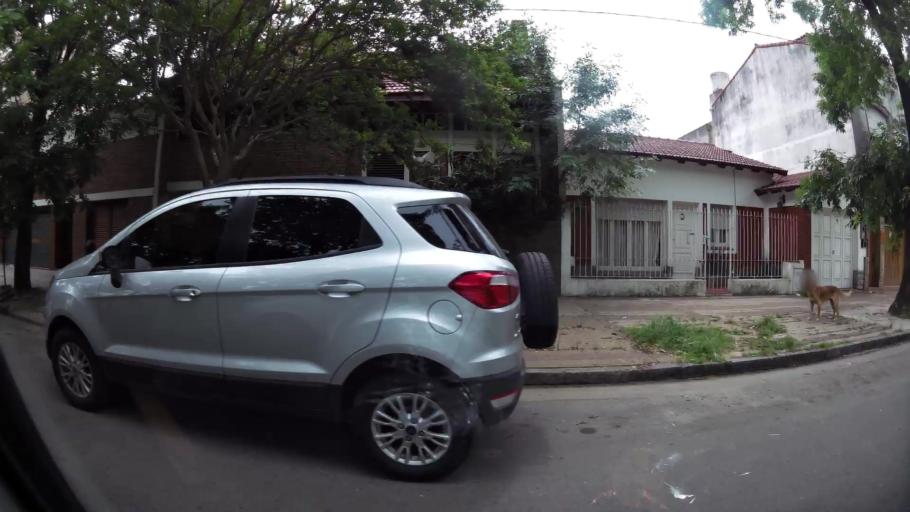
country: AR
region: Buenos Aires
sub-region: Partido de La Plata
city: La Plata
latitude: -34.9417
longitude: -57.9644
